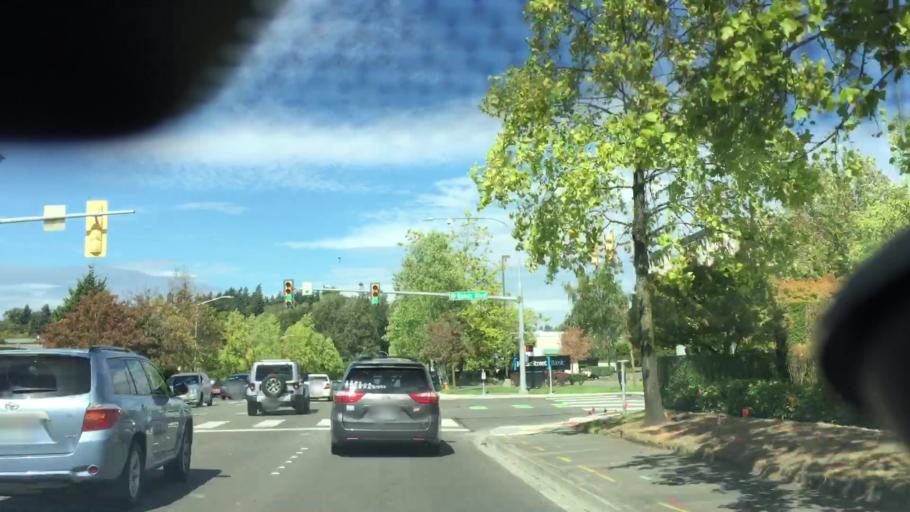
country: US
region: Washington
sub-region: King County
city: Tukwila
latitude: 47.4579
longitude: -122.2499
